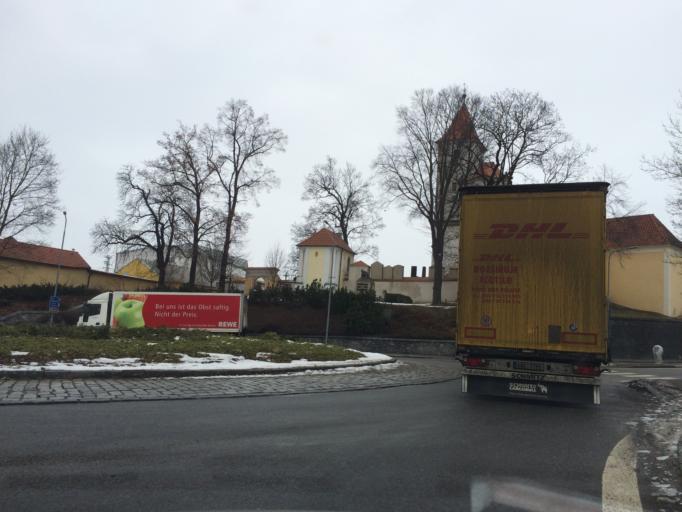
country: CZ
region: Jihocesky
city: Strakonice
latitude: 49.2540
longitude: 13.9146
